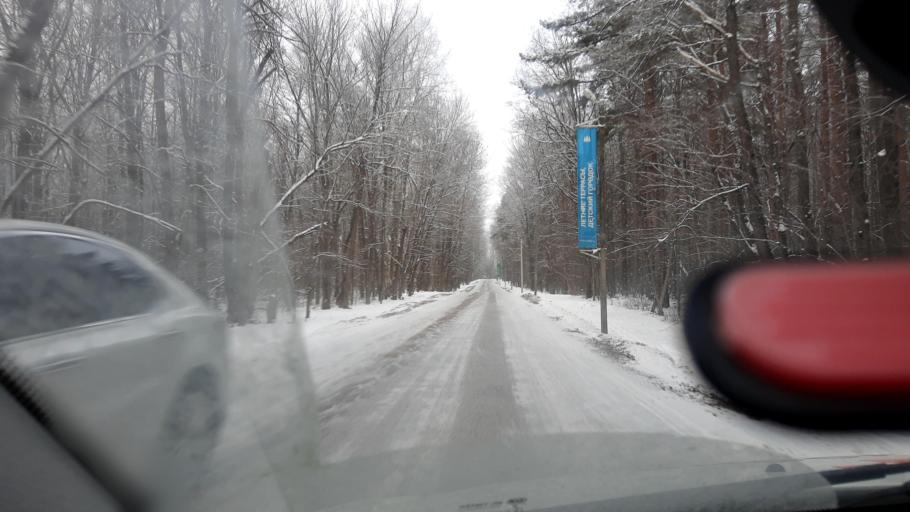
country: RU
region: Bashkortostan
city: Ufa
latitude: 54.7038
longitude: 55.9244
